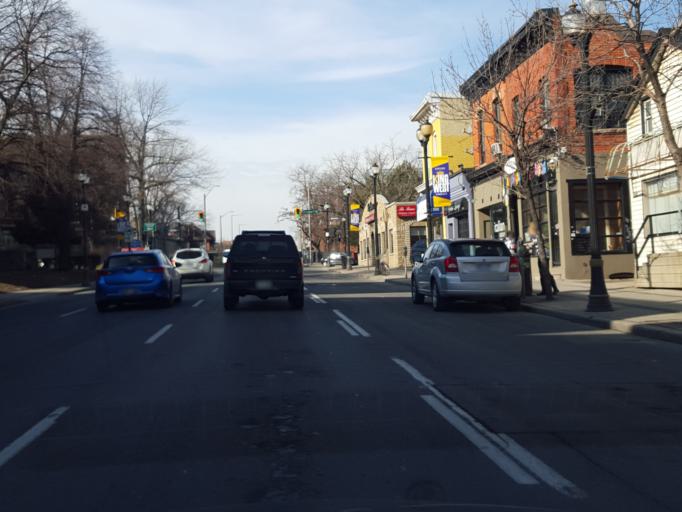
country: CA
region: Ontario
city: Hamilton
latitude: 43.2591
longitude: -79.8778
